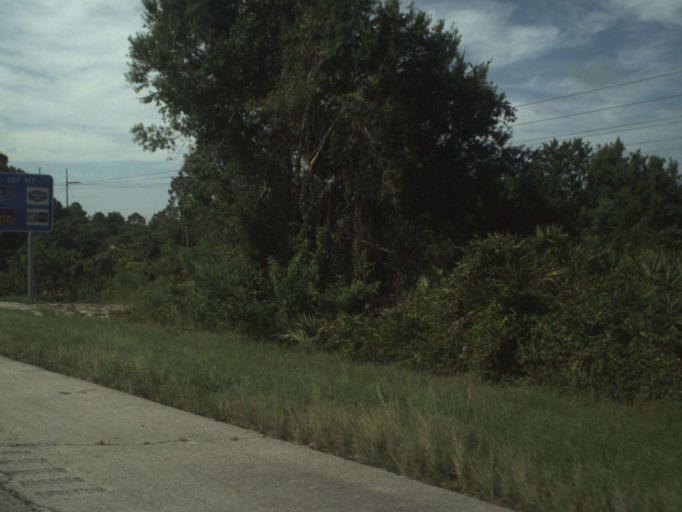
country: US
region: Florida
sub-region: Indian River County
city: West Vero Corridor
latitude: 27.6621
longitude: -80.5282
